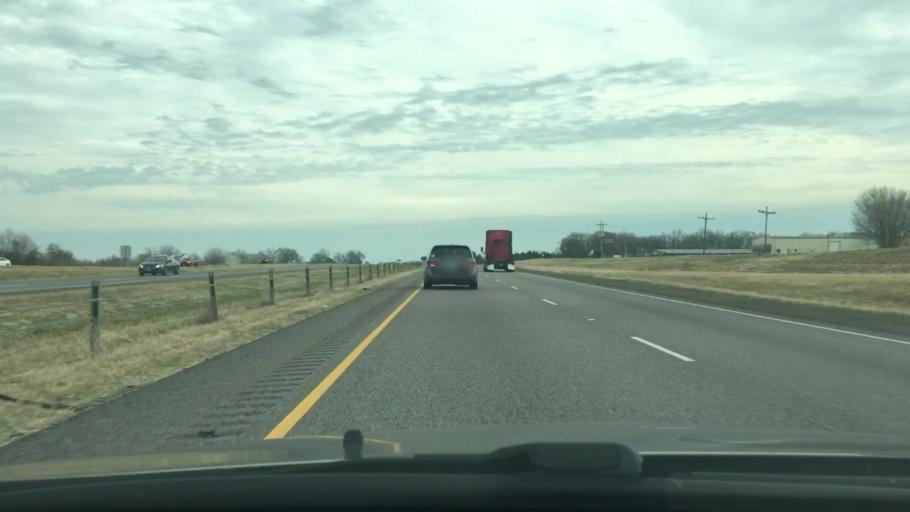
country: US
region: Texas
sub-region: Madison County
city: Madisonville
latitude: 30.9644
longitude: -95.8817
